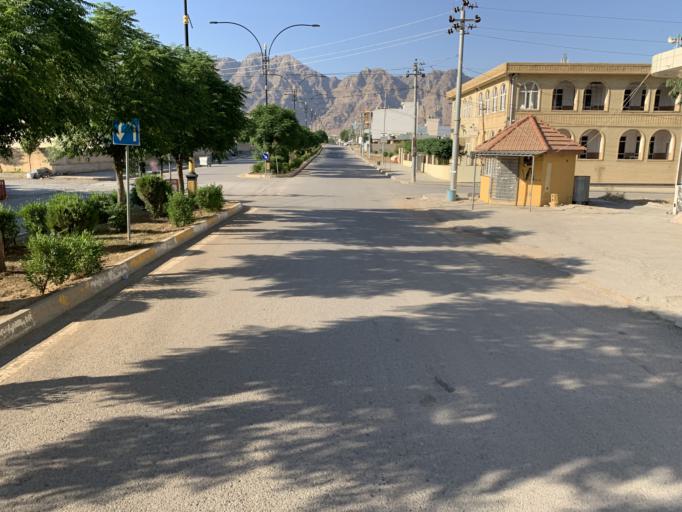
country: IQ
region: As Sulaymaniyah
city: Raniye
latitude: 36.2432
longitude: 44.8728
